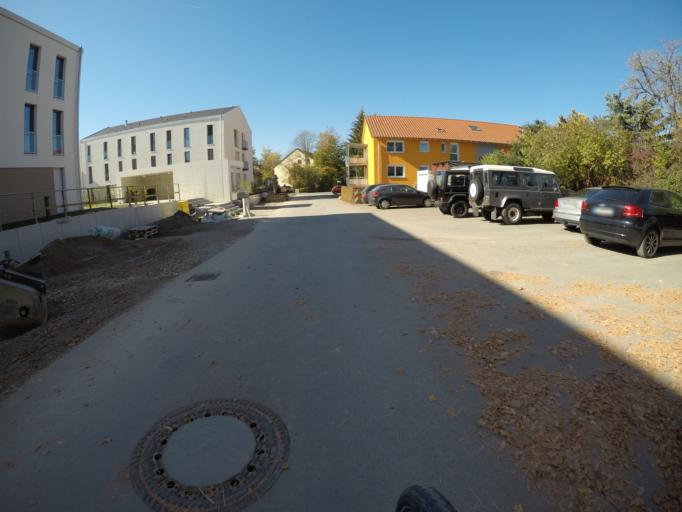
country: DE
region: Baden-Wuerttemberg
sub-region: Tuebingen Region
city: Tuebingen
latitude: 48.5213
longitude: 9.0294
